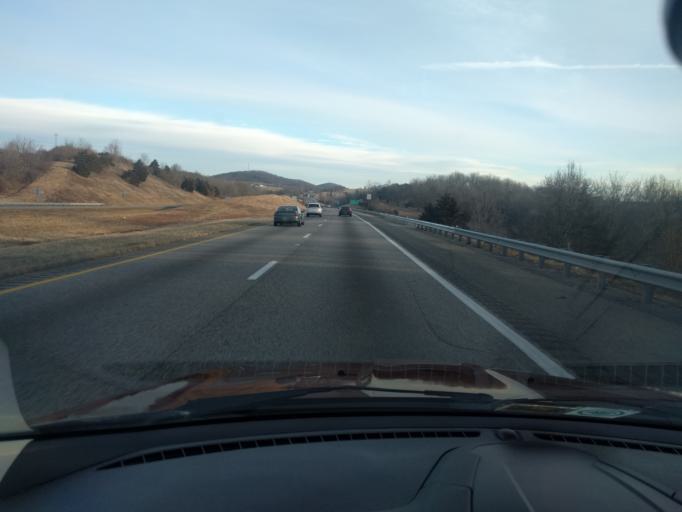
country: US
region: Virginia
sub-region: Augusta County
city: Jolivue
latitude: 38.0846
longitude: -79.0792
